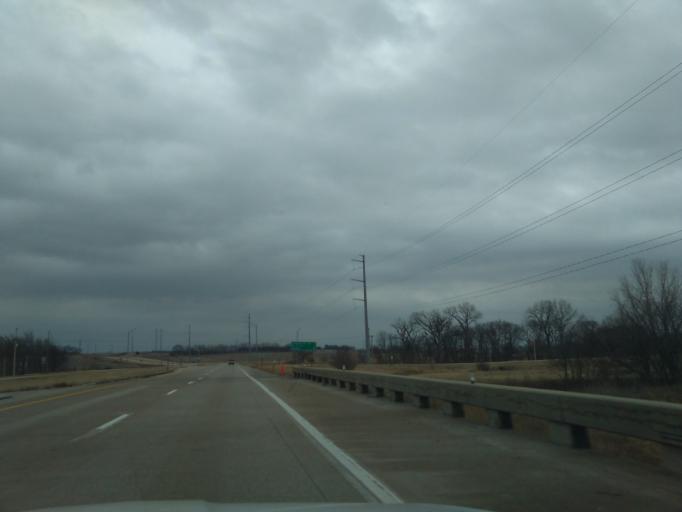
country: US
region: Nebraska
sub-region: Otoe County
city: Syracuse
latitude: 40.6764
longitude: -96.0324
